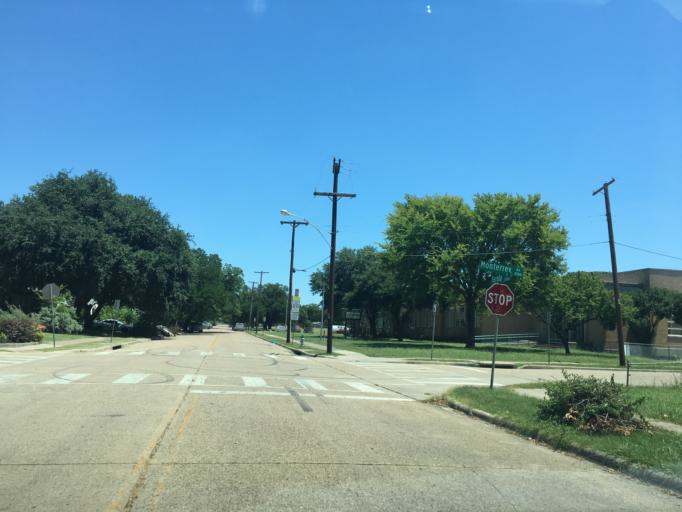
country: US
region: Texas
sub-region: Dallas County
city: Garland
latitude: 32.8454
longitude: -96.6770
